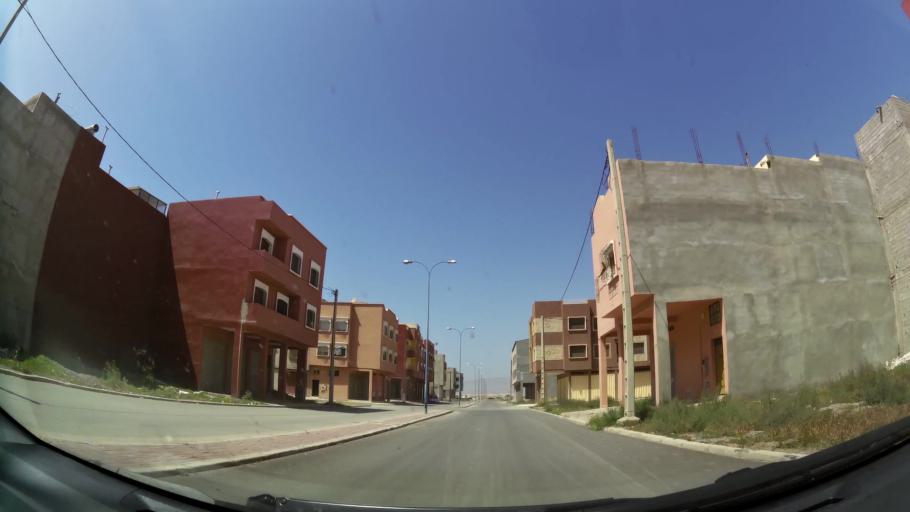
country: MA
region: Souss-Massa-Draa
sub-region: Inezgane-Ait Mellou
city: Inezgane
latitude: 30.3470
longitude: -9.5184
